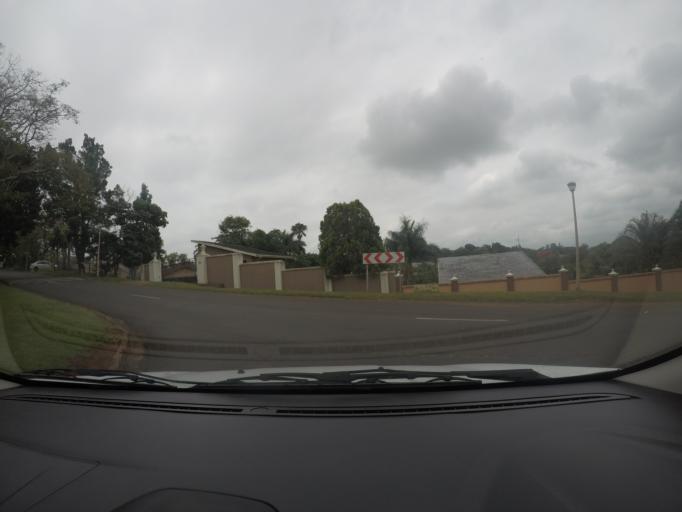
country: ZA
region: KwaZulu-Natal
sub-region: uThungulu District Municipality
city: Empangeni
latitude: -28.7539
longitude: 31.8876
